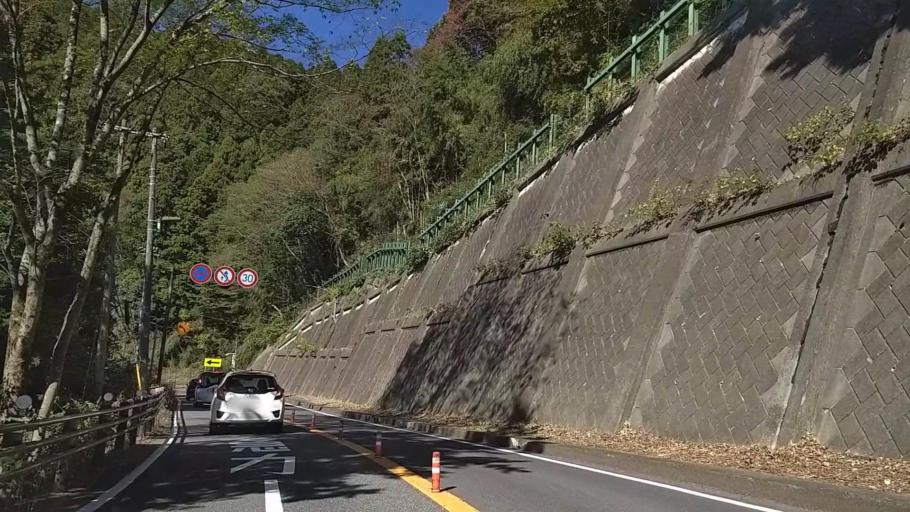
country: JP
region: Yamanashi
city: Uenohara
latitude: 35.6186
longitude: 139.2209
